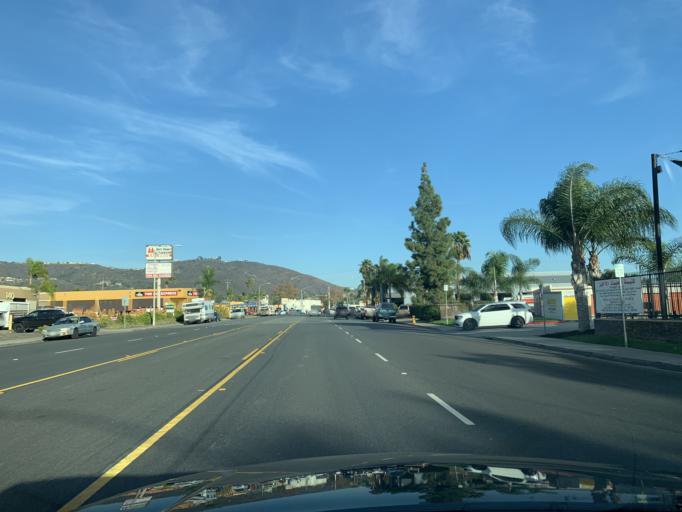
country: US
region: California
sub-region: San Diego County
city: Santee
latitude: 32.8186
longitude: -116.9646
